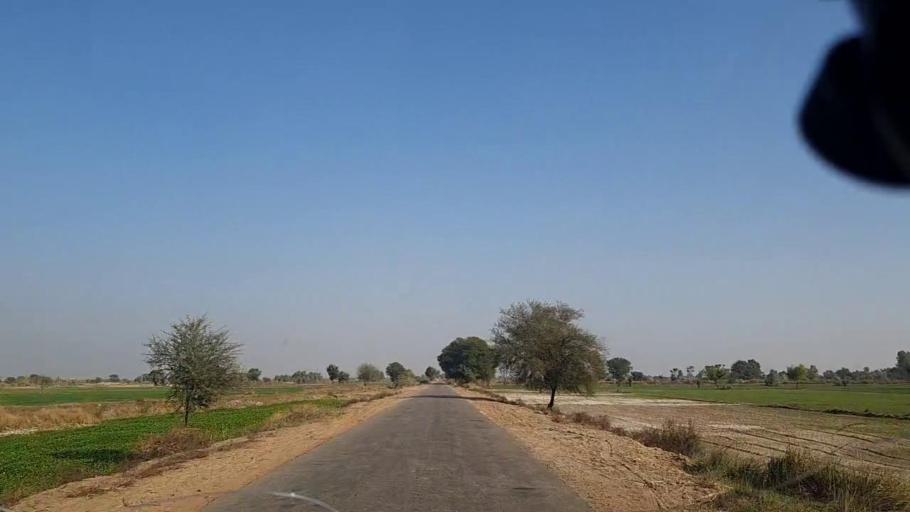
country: PK
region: Sindh
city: Khanpur
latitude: 27.6882
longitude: 69.5021
